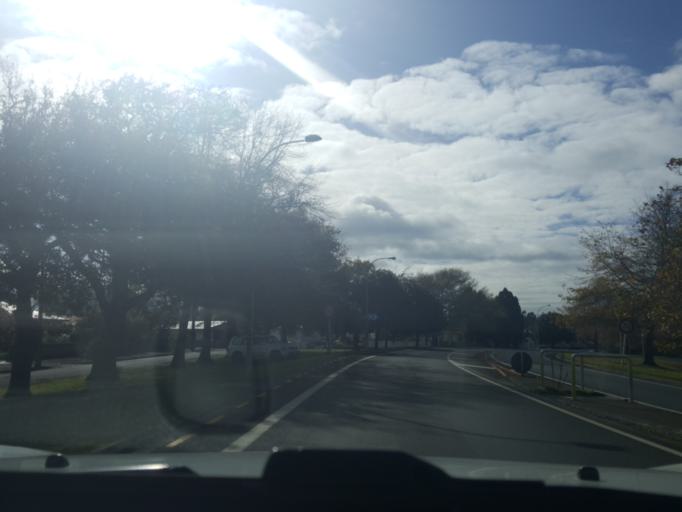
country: NZ
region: Waikato
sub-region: Hauraki District
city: Waihi
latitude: -37.3928
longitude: 175.8325
